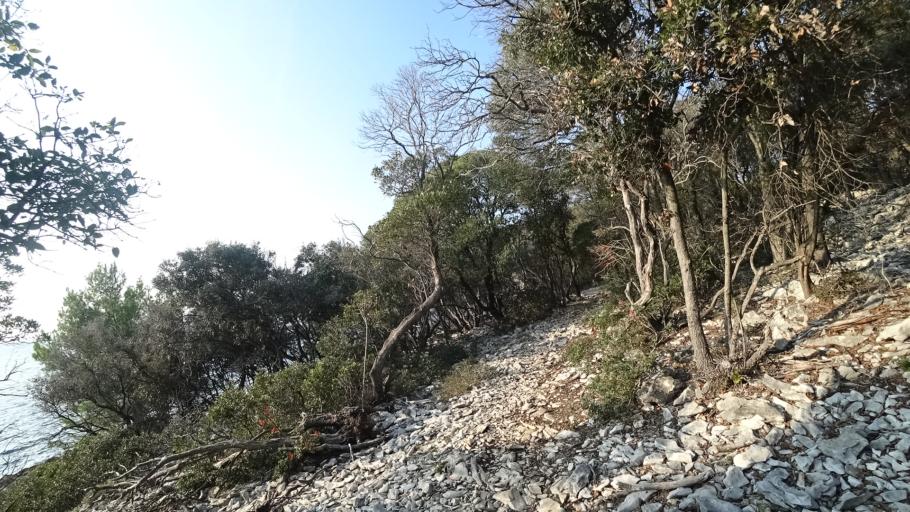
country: HR
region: Primorsko-Goranska
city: Mali Losinj
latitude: 44.5124
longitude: 14.4742
